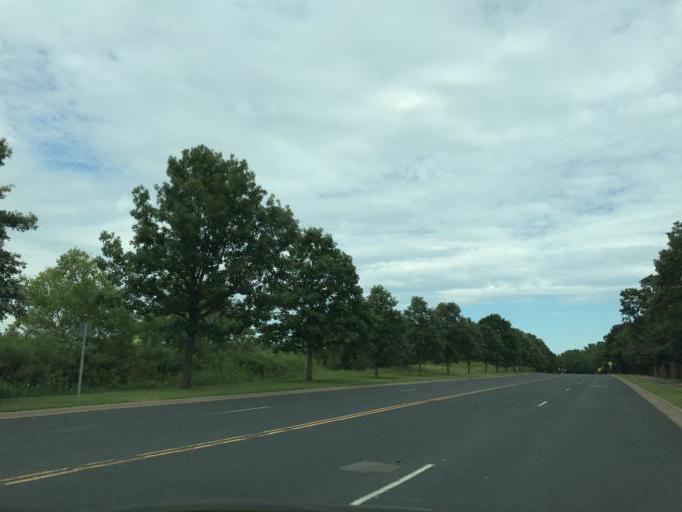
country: US
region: Minnesota
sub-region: Hennepin County
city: Osseo
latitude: 45.0853
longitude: -93.4158
